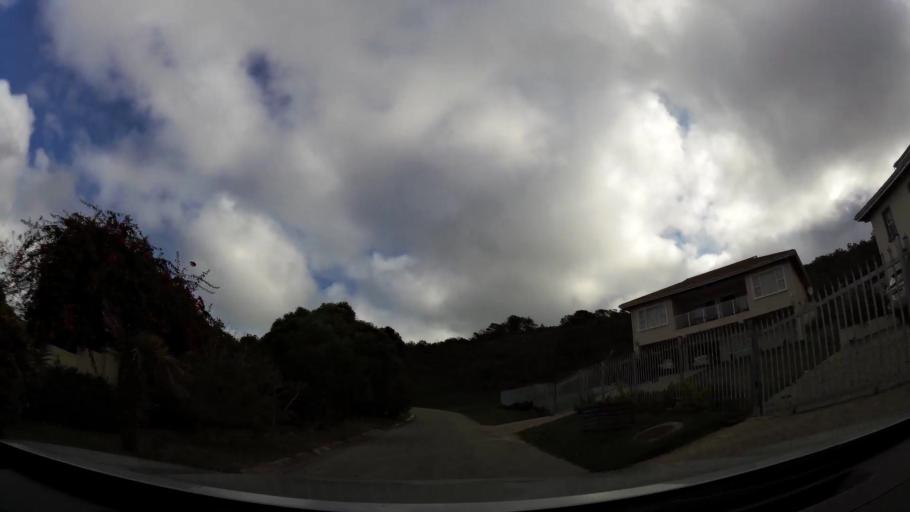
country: ZA
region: Western Cape
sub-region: Eden District Municipality
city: Plettenberg Bay
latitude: -34.0802
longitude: 23.3622
